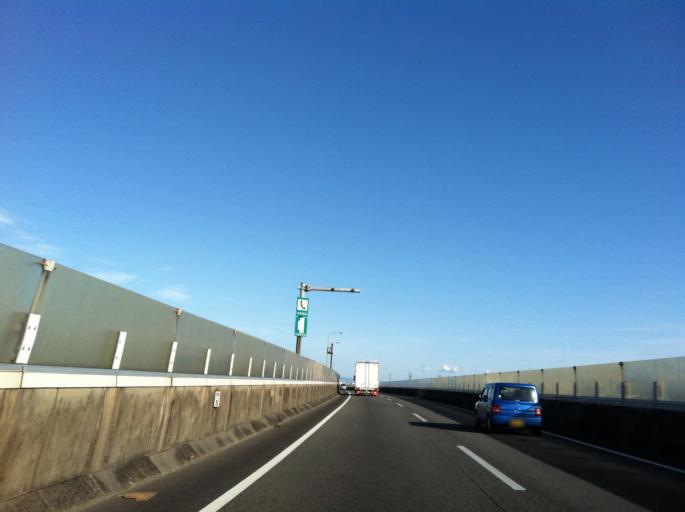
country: JP
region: Shizuoka
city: Shizuoka-shi
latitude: 35.0088
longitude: 138.4248
